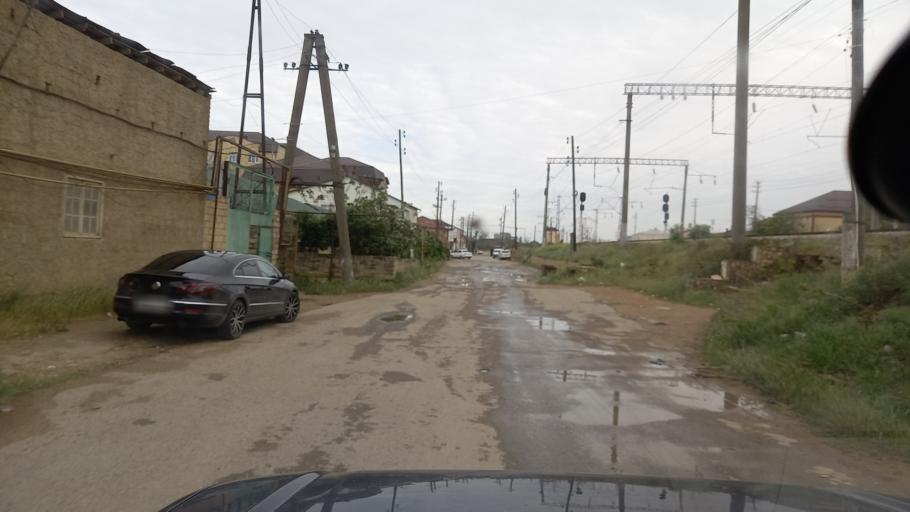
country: RU
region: Dagestan
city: Derbent
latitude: 42.0665
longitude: 48.3028
